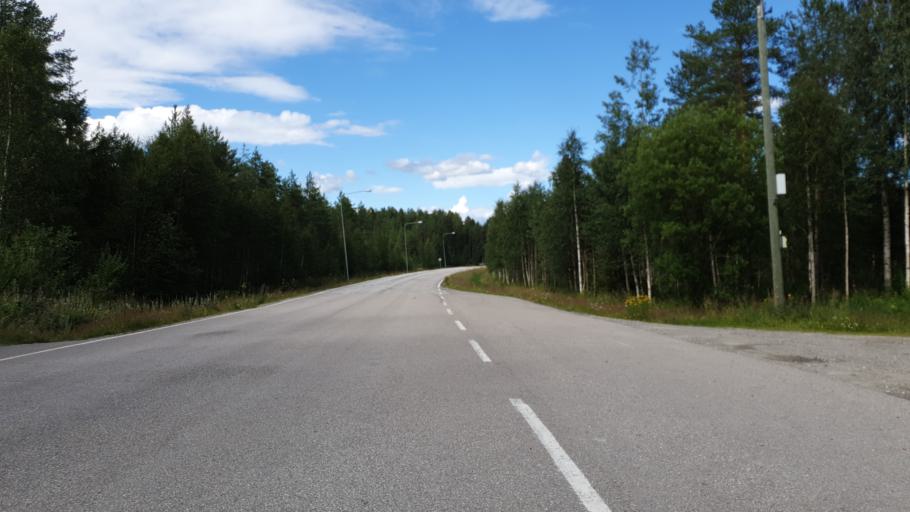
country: FI
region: Kainuu
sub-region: Kehys-Kainuu
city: Kuhmo
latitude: 64.1158
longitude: 29.5272
